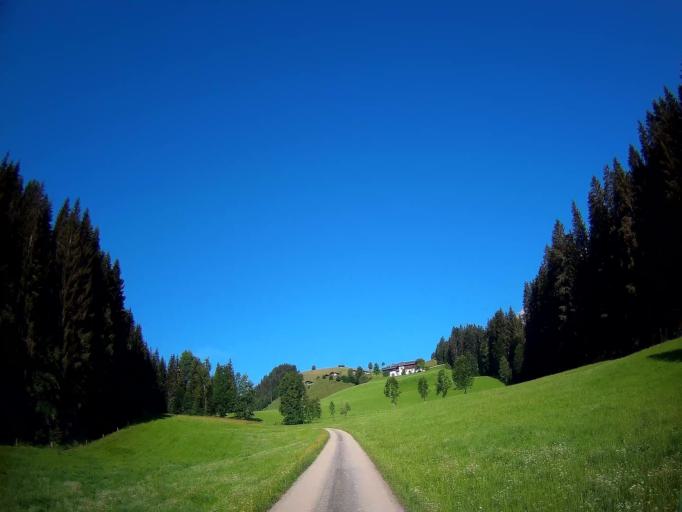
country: AT
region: Salzburg
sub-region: Politischer Bezirk Zell am See
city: Leogang
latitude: 47.4507
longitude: 12.7884
